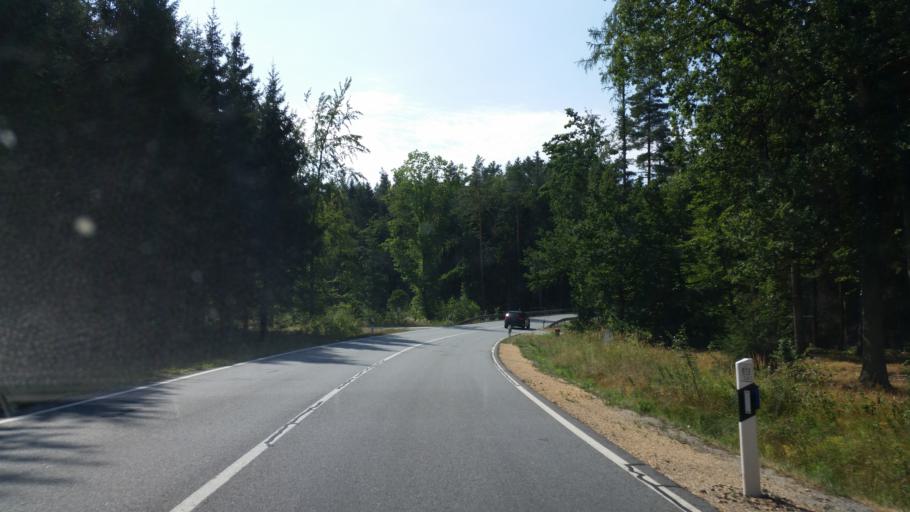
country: DE
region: Saxony
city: Grosshennersdorf
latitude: 50.9752
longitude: 14.7538
